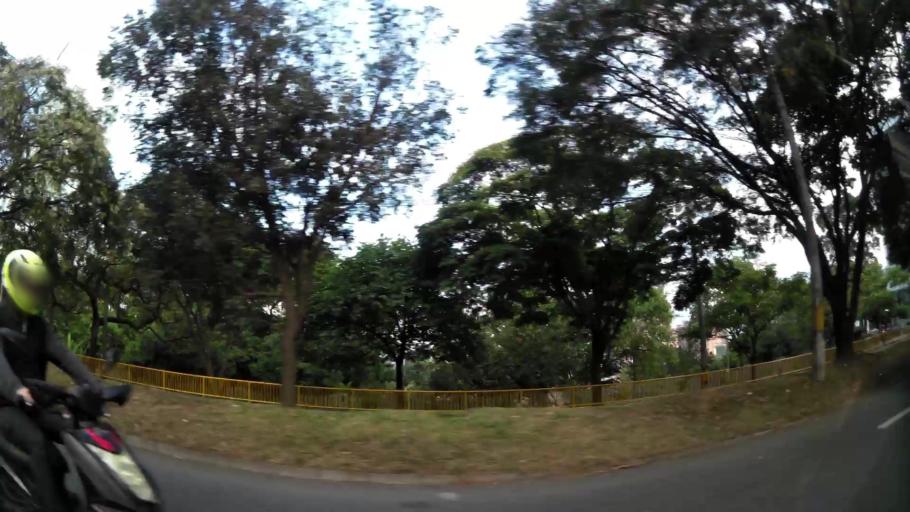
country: CO
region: Antioquia
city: Medellin
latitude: 6.2190
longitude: -75.5696
